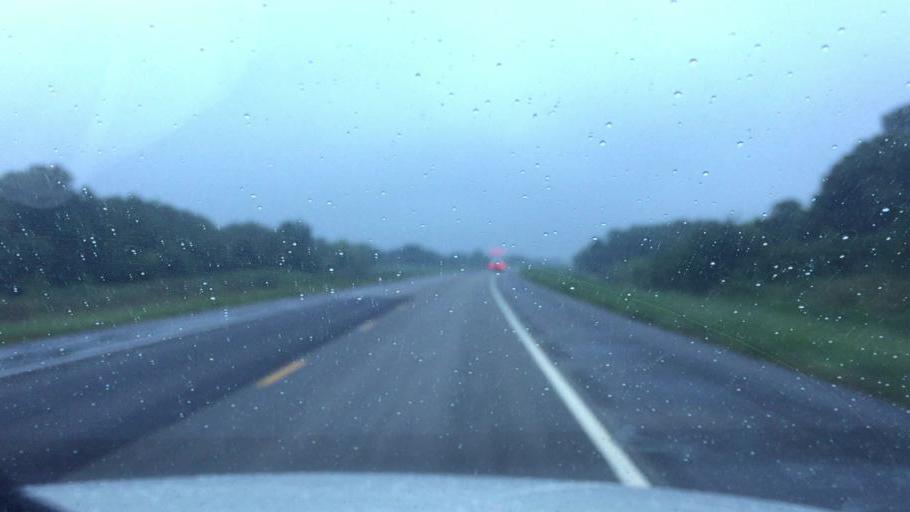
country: US
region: Kansas
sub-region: Montgomery County
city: Cherryvale
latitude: 37.4450
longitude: -95.4842
